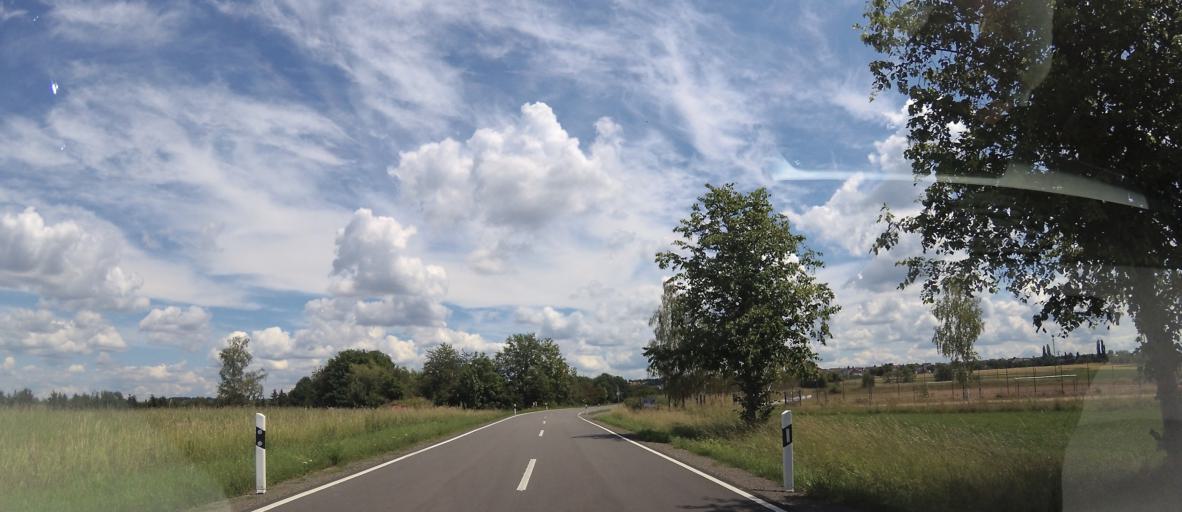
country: DE
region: Rheinland-Pfalz
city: Vinningen
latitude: 49.1640
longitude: 7.5389
